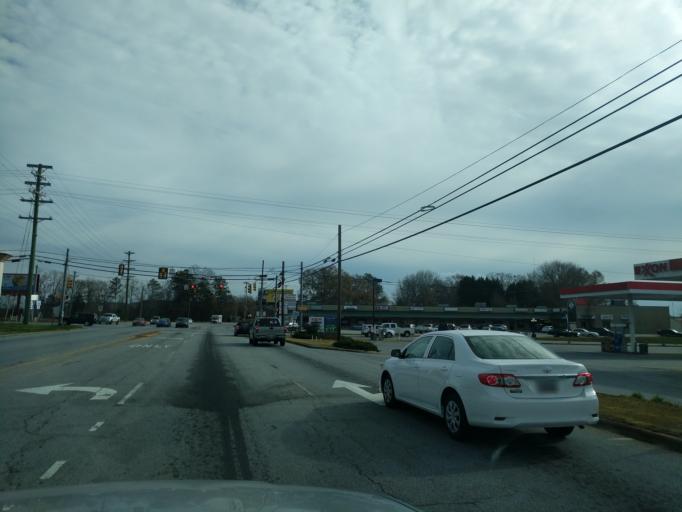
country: US
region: South Carolina
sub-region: Oconee County
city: Seneca
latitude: 34.7109
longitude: -82.9957
